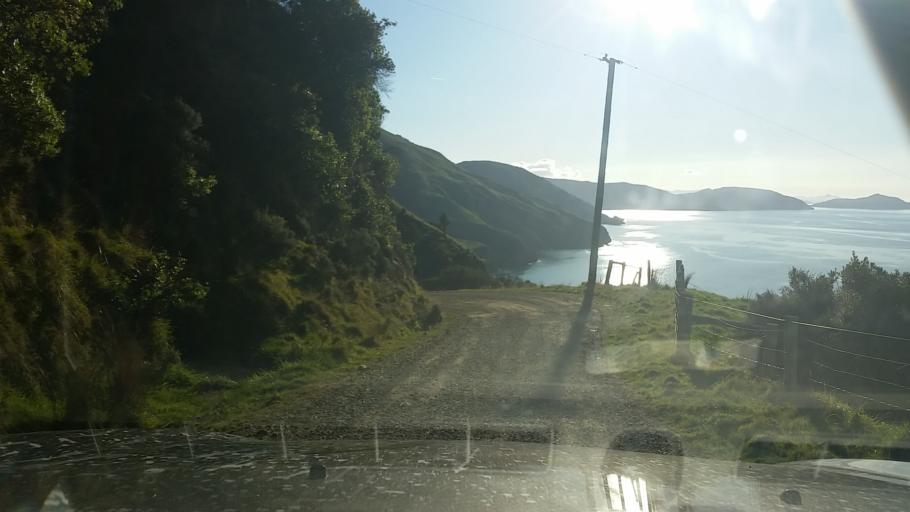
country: NZ
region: Marlborough
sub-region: Marlborough District
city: Picton
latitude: -41.0233
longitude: 174.1447
